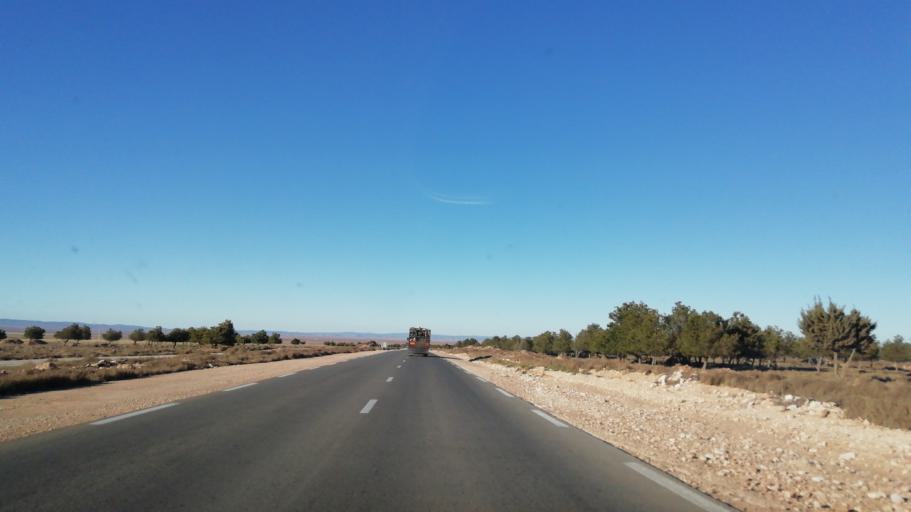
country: DZ
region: Tlemcen
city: Sebdou
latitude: 34.3165
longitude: -1.2628
